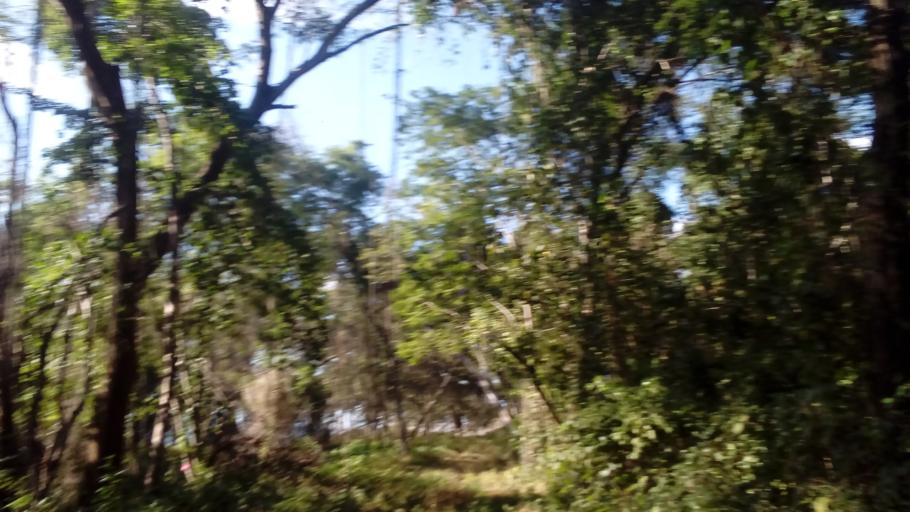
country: CR
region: Guanacaste
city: Sardinal
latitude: 10.3943
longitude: -85.8338
